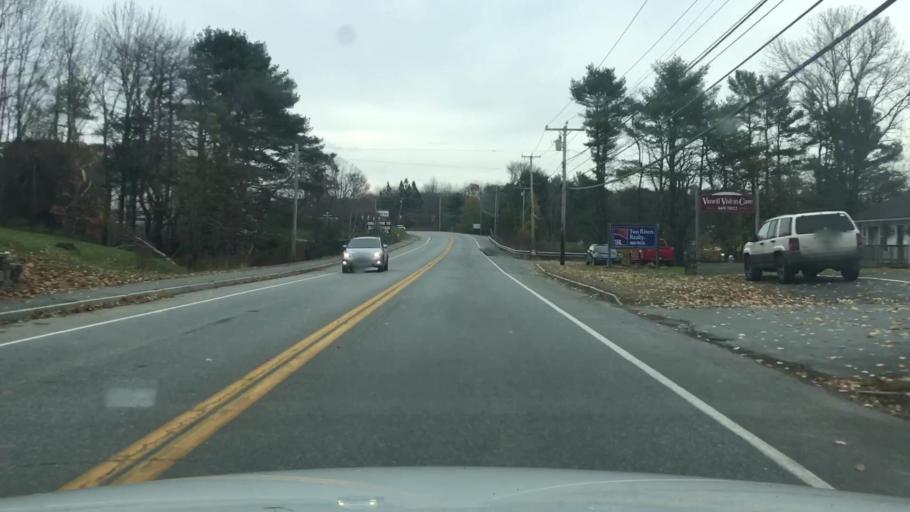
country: US
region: Maine
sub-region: Hancock County
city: Bucksport
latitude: 44.5697
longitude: -68.7746
